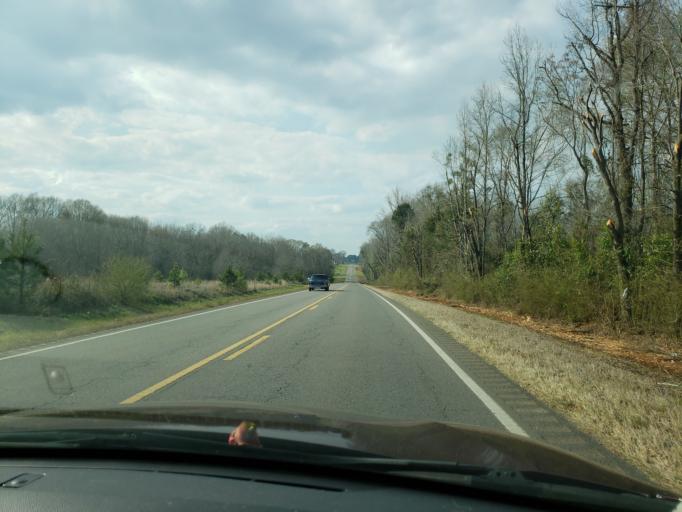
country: US
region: Alabama
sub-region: Hale County
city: Greensboro
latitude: 32.7087
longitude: -87.6093
